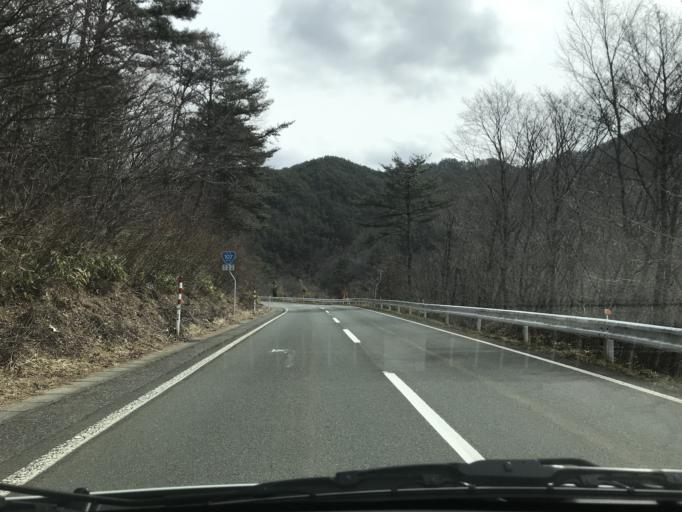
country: JP
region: Iwate
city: Tono
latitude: 39.2978
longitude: 141.3644
